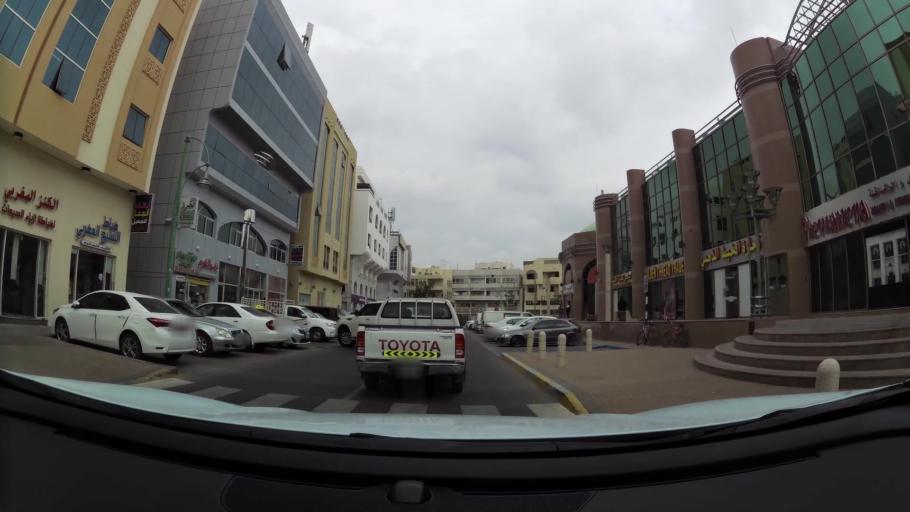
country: AE
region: Abu Dhabi
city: Al Ain
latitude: 24.2240
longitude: 55.7664
